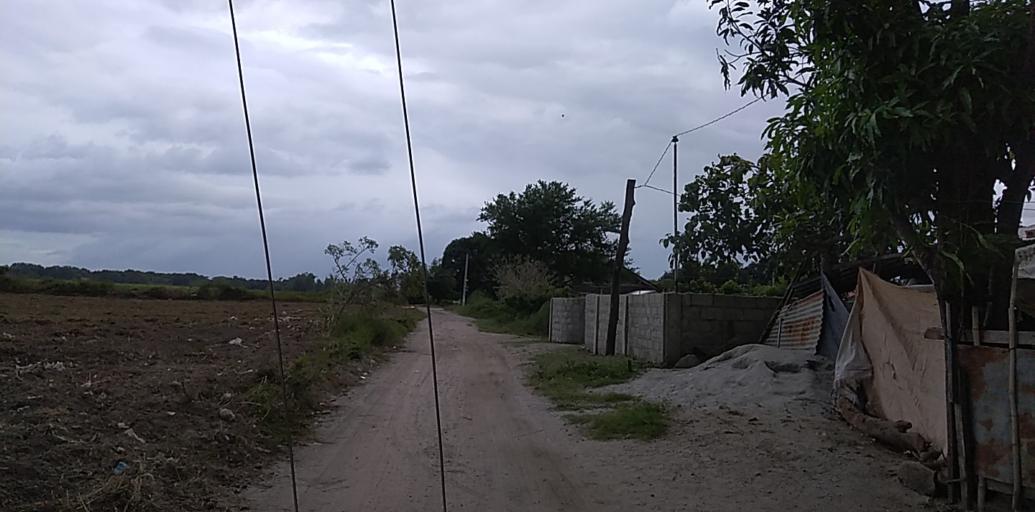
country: PH
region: Central Luzon
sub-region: Province of Pampanga
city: Pio
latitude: 15.0489
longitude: 120.5388
